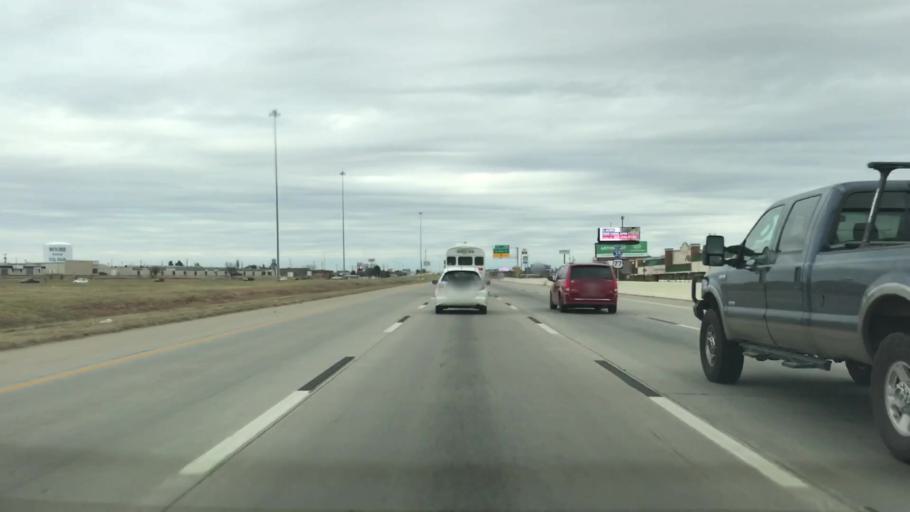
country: US
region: Oklahoma
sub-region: Cleveland County
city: Moore
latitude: 35.3570
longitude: -97.4946
